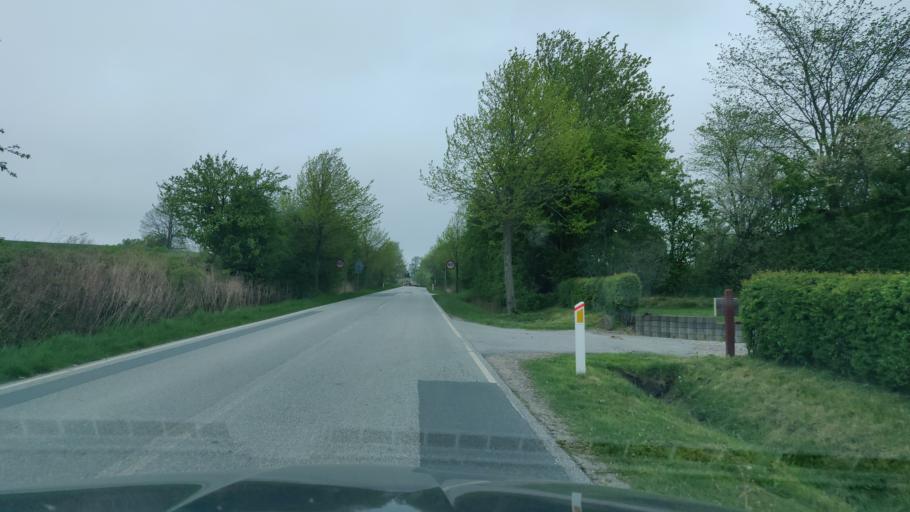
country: DK
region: South Denmark
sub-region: Sonderborg Kommune
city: Guderup
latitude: 54.9902
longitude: 9.8887
